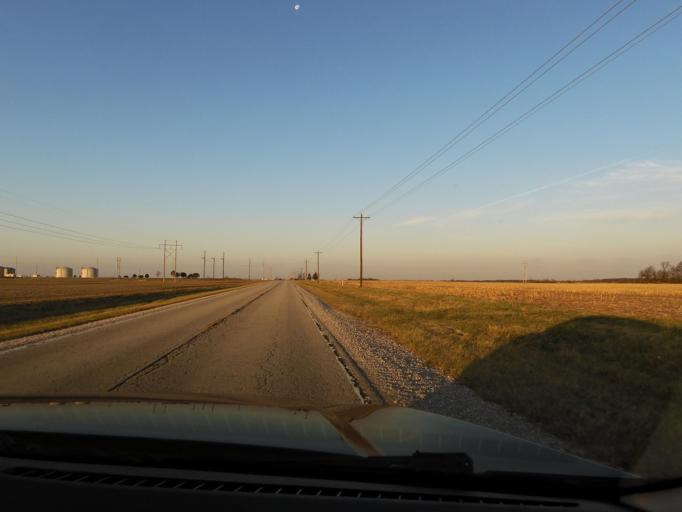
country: US
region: Illinois
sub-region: Marion County
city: Salem
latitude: 38.7653
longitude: -89.0062
